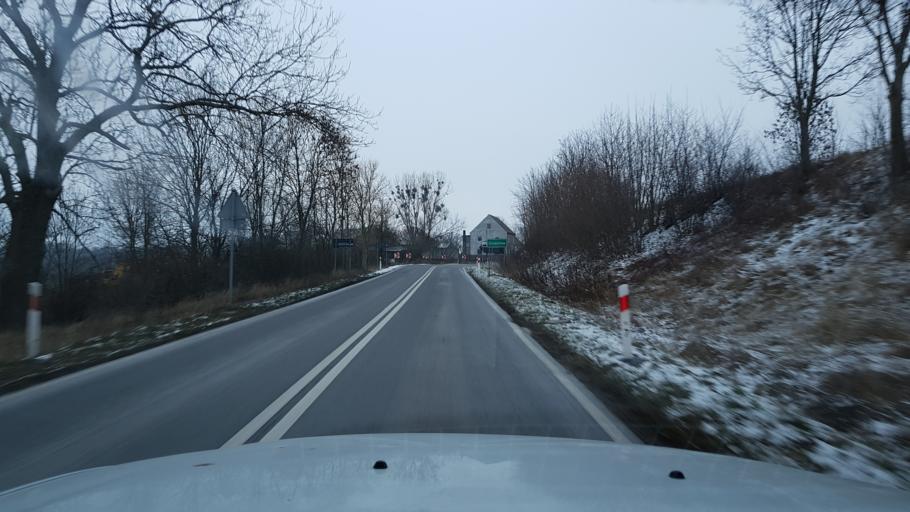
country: PL
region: West Pomeranian Voivodeship
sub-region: Powiat gryfinski
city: Cedynia
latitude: 52.8830
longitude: 14.2818
